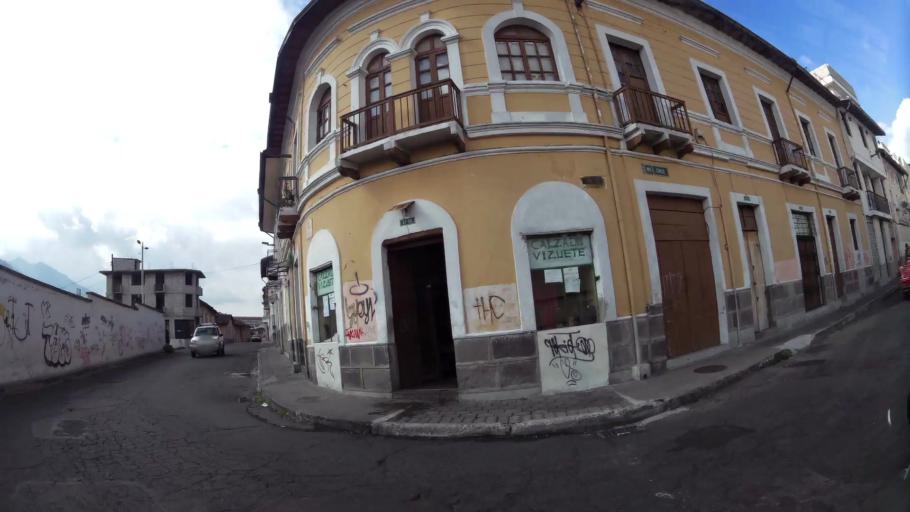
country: EC
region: Pichincha
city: Quito
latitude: -0.2226
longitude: -78.5076
